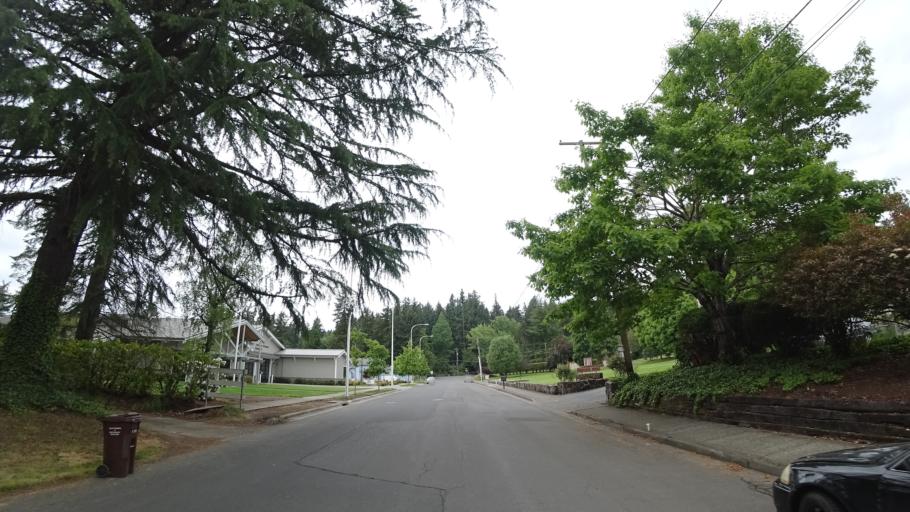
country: US
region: Oregon
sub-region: Washington County
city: West Slope
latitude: 45.4947
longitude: -122.7825
